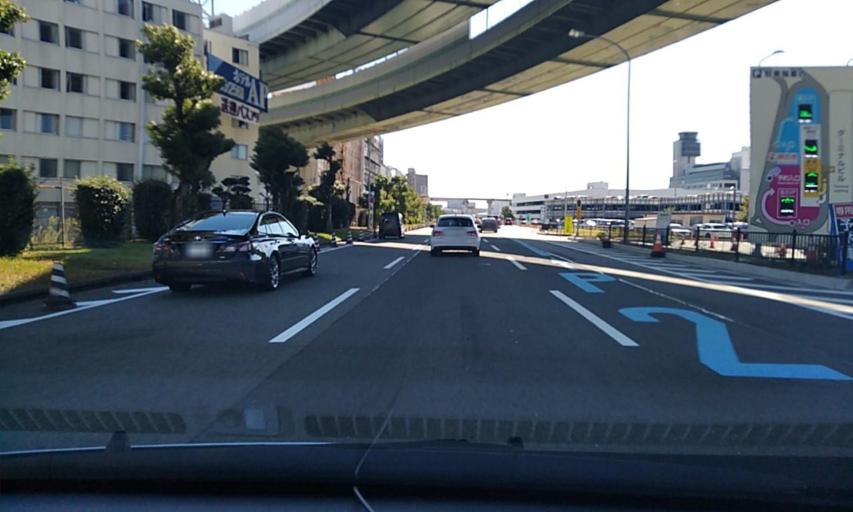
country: JP
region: Osaka
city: Toyonaka
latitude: 34.7929
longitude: 135.4424
